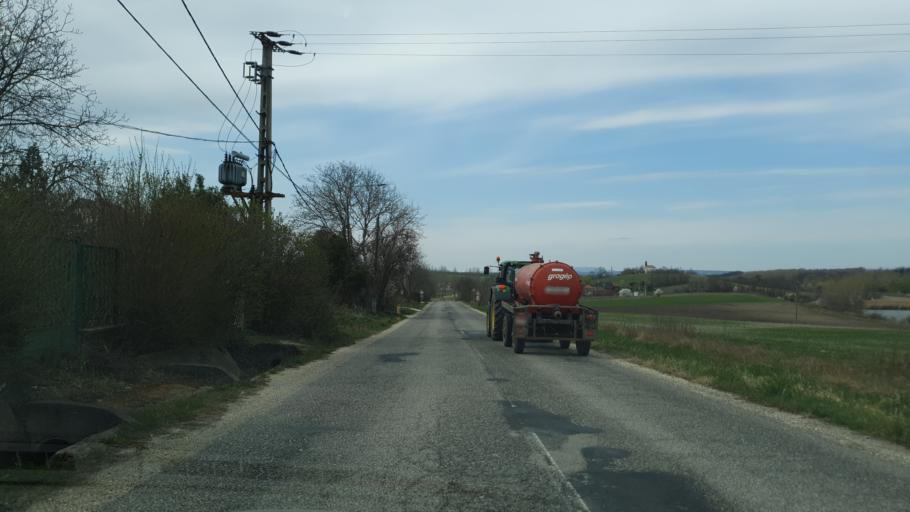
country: HU
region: Fejer
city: Etyek
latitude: 47.4530
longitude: 18.7355
